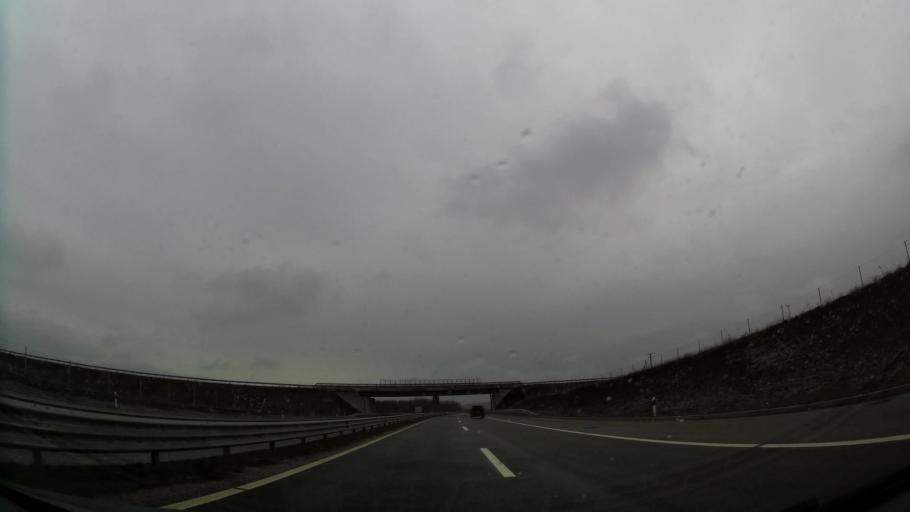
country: XK
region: Ferizaj
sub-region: Komuna e Ferizajt
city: Ferizaj
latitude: 42.3507
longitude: 21.2047
